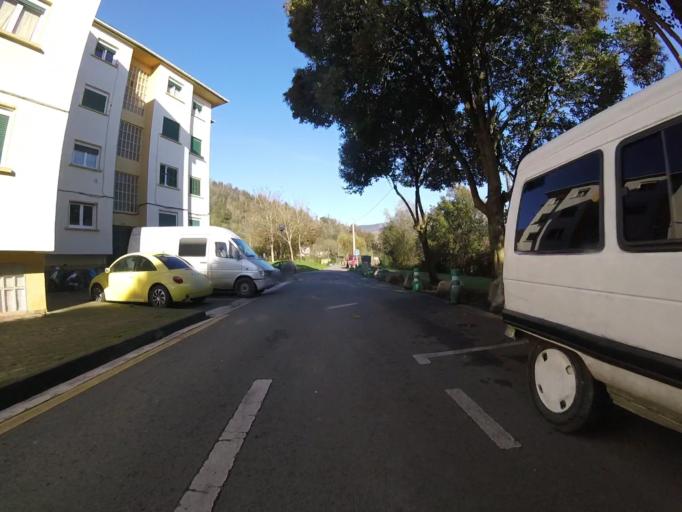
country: ES
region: Basque Country
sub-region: Provincia de Guipuzcoa
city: Usurbil
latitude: 43.2675
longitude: -2.0568
